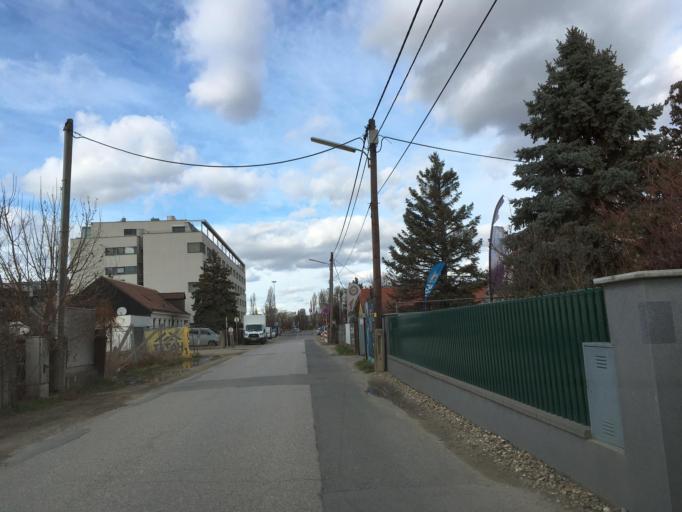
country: AT
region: Lower Austria
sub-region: Politischer Bezirk Ganserndorf
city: Gross-Enzersdorf
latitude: 48.2141
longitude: 16.5040
